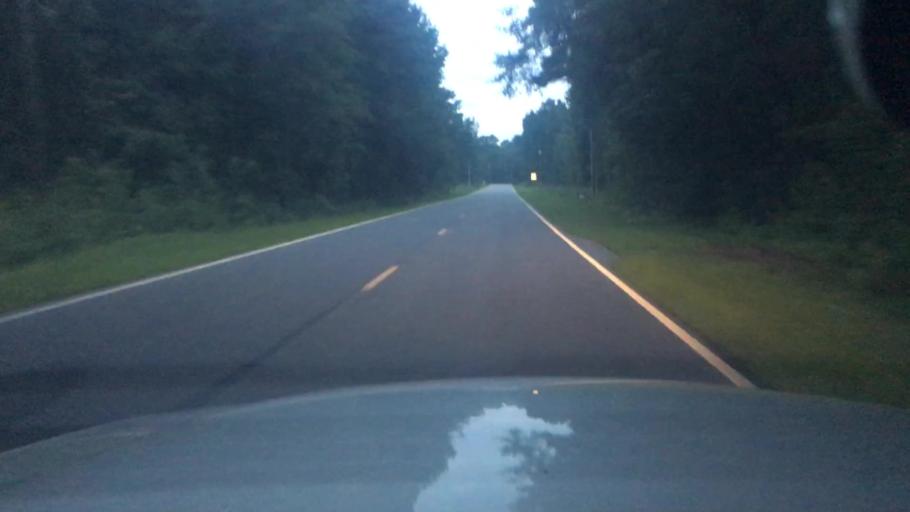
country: US
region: North Carolina
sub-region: Cumberland County
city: Hope Mills
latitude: 34.9588
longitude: -78.9314
